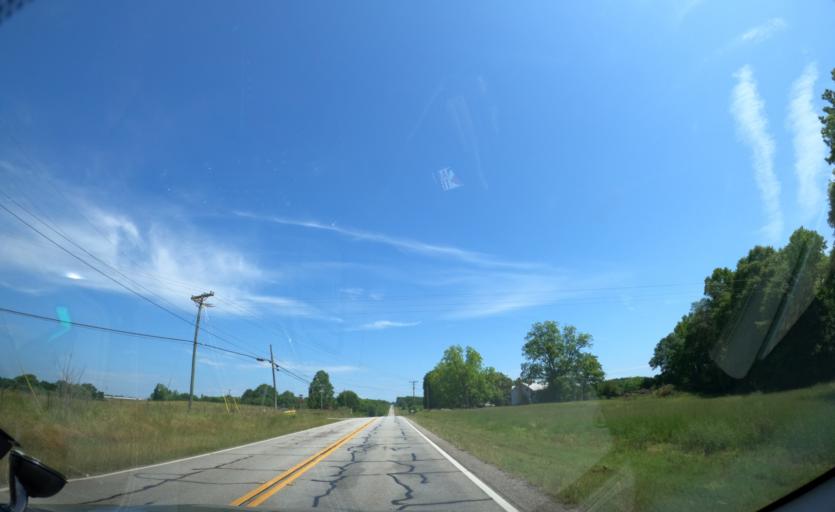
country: US
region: Georgia
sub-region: Hart County
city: Hartwell
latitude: 34.2747
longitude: -82.8990
